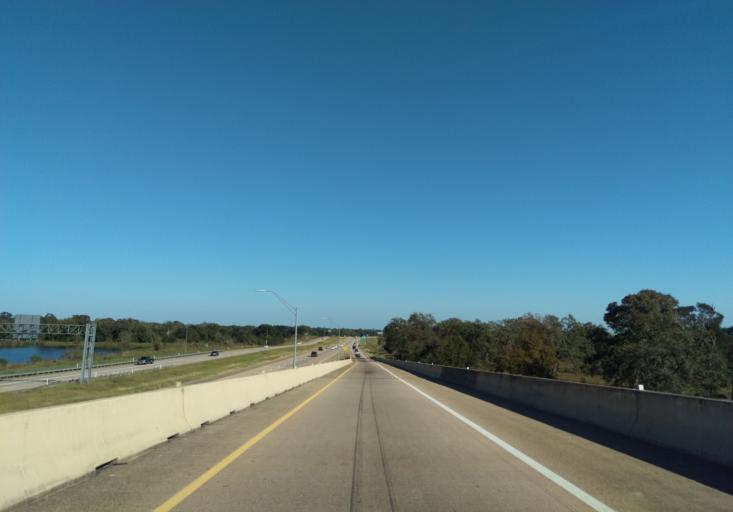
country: US
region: Texas
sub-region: Waller County
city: Hempstead
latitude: 30.1134
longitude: -96.0706
